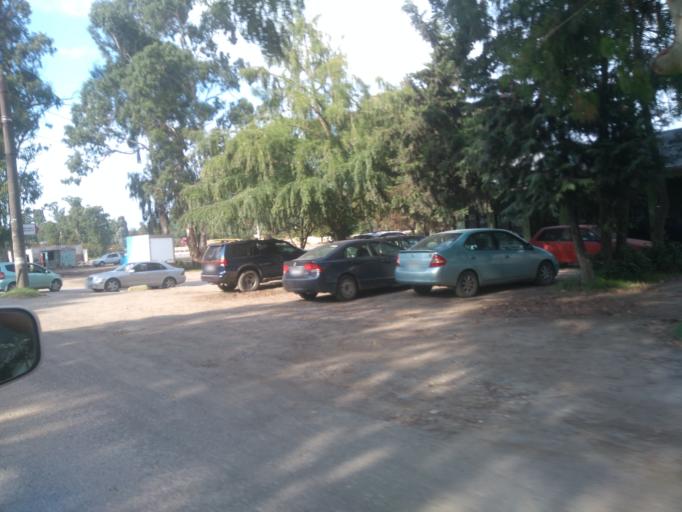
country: GE
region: Ajaria
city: Khelvachauri
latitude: 41.5948
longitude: 41.6421
